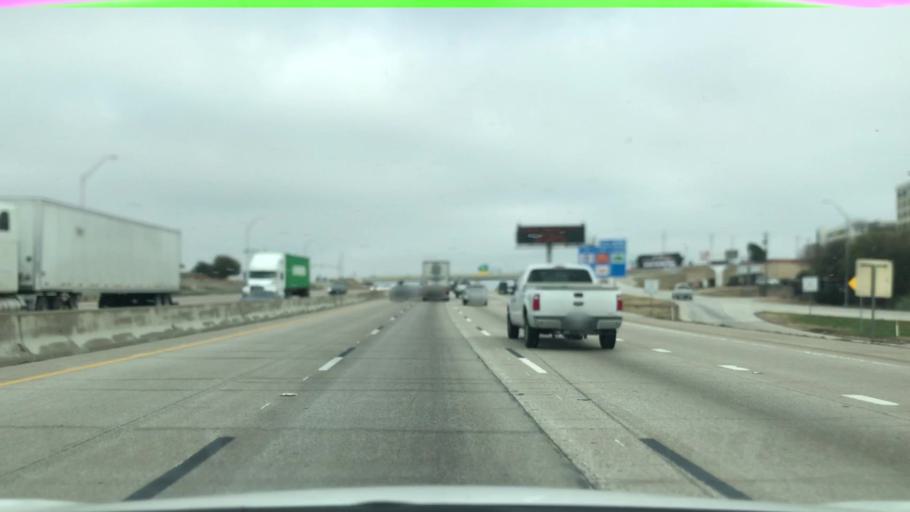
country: US
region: Texas
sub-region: Rockwall County
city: Rockwall
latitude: 32.8942
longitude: -96.4799
